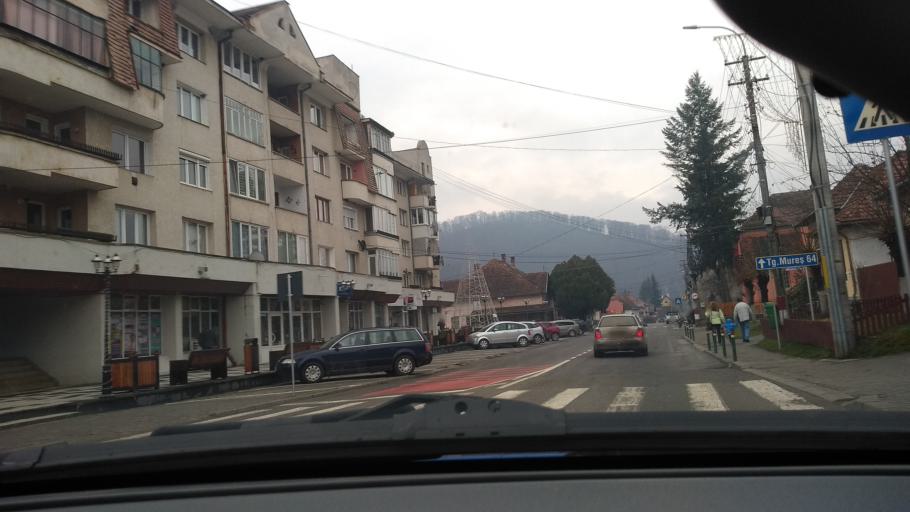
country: RO
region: Mures
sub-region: Oras Sovata
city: Sovata
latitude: 46.5972
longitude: 25.0709
